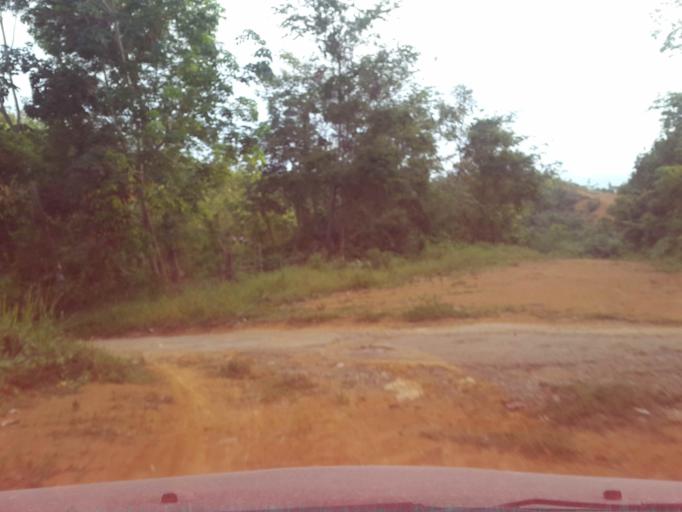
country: MY
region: Sarawak
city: Simanggang
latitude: 1.0311
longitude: 111.9115
